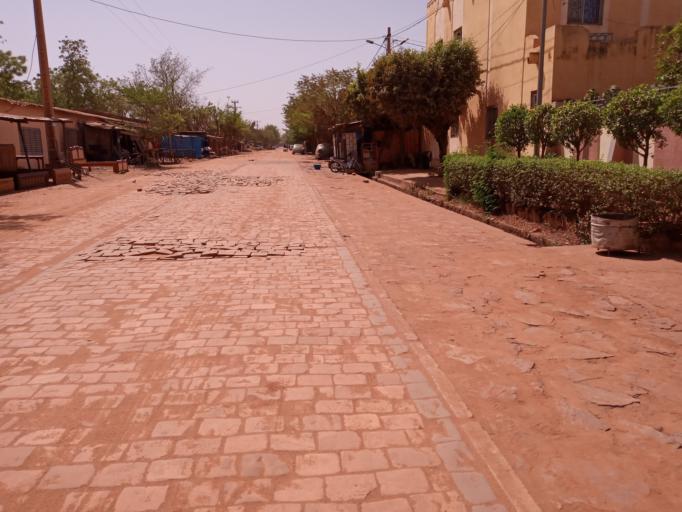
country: ML
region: Bamako
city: Bamako
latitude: 12.5871
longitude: -7.9572
